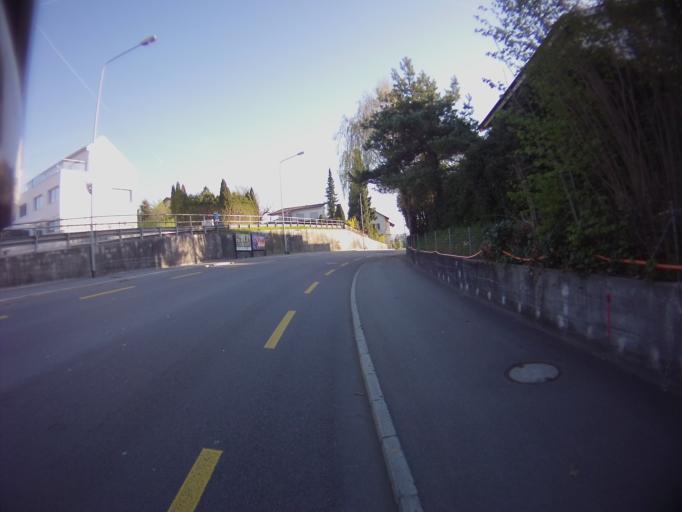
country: CH
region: Zurich
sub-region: Bezirk Affoltern
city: Hedingen
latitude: 47.3023
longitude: 8.4487
